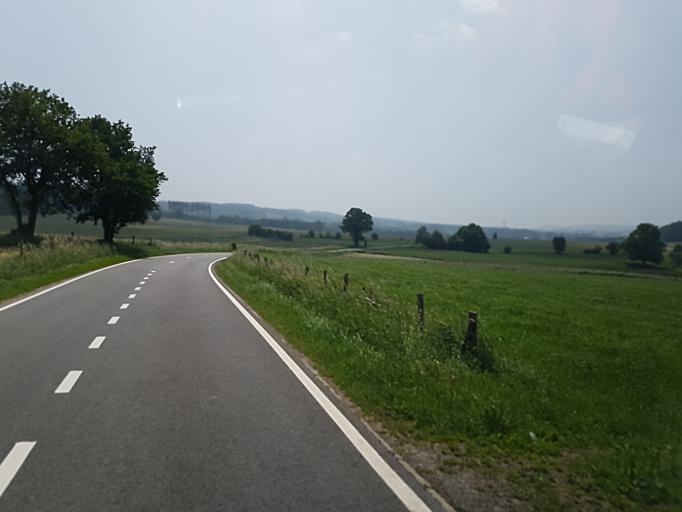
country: BE
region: Wallonia
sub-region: Province du Luxembourg
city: Manhay
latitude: 50.3134
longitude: 5.7257
